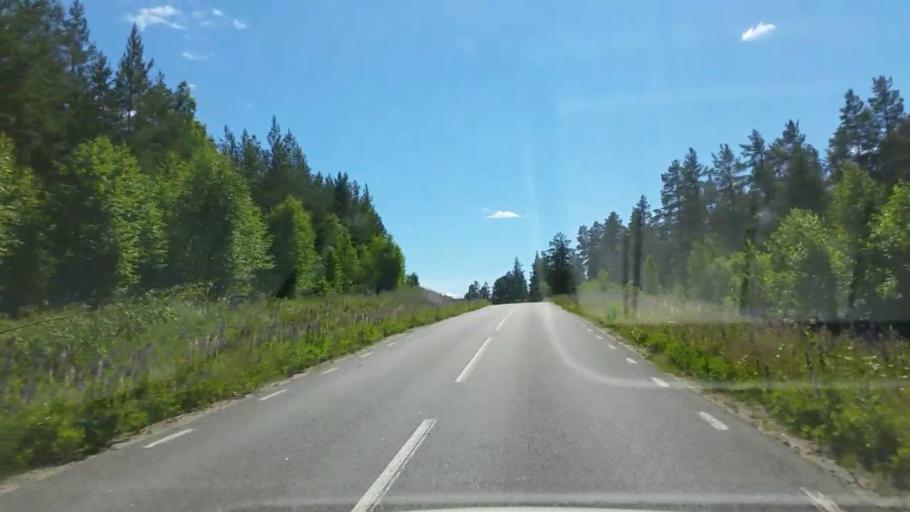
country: SE
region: Gaevleborg
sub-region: Ljusdals Kommun
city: Farila
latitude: 61.7284
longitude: 15.7257
